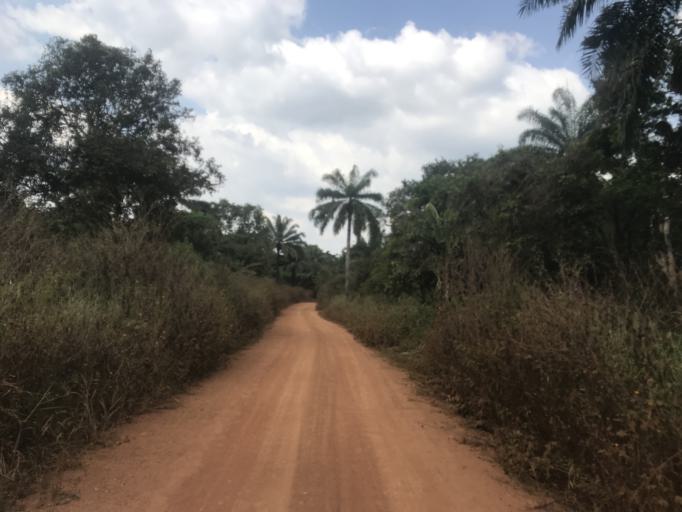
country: NG
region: Osun
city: Inisa
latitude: 7.8685
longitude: 4.3827
